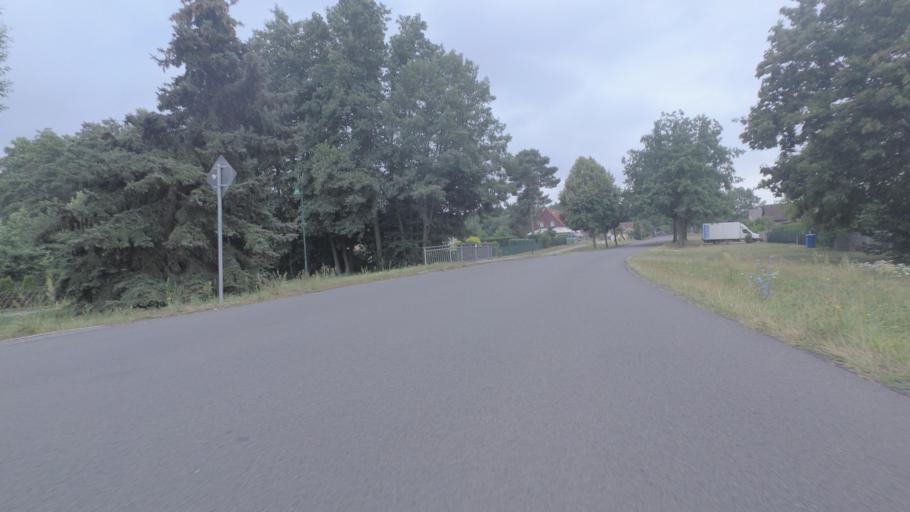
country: DE
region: Brandenburg
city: Wustermark
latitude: 52.5228
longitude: 12.9818
